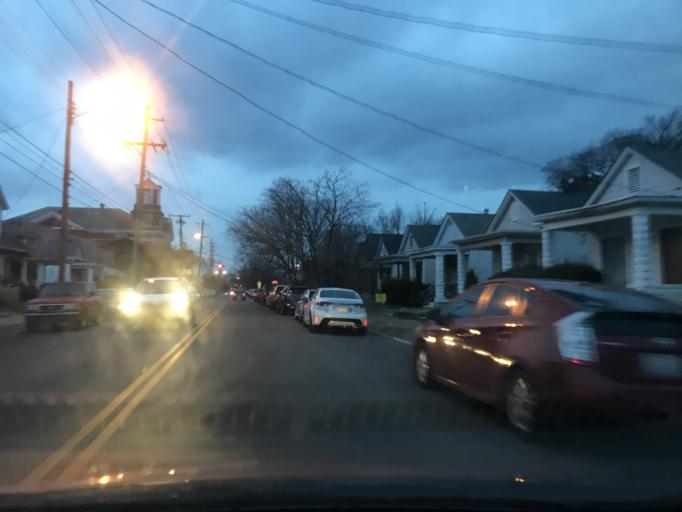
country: US
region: Kentucky
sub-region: Jefferson County
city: Audubon Park
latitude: 38.2223
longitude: -85.7383
